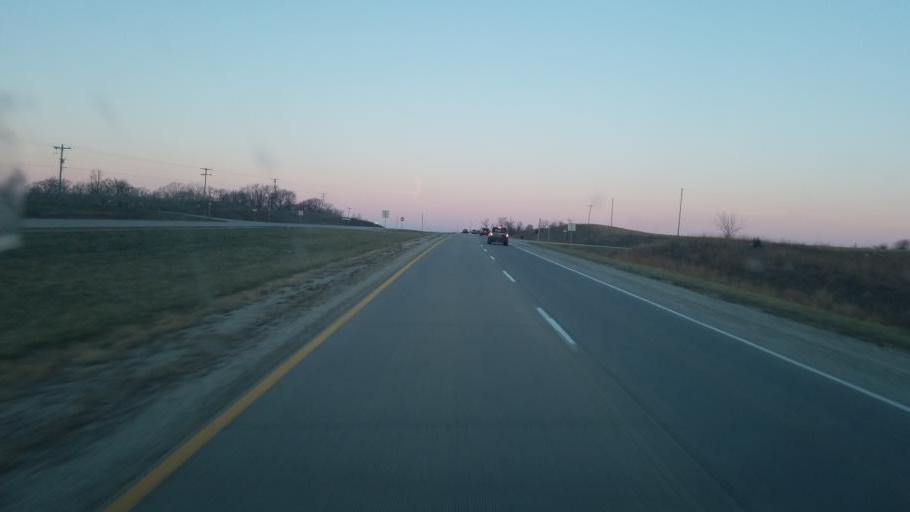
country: US
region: Iowa
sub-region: Henry County
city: Mount Pleasant
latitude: 40.9744
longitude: -91.6586
